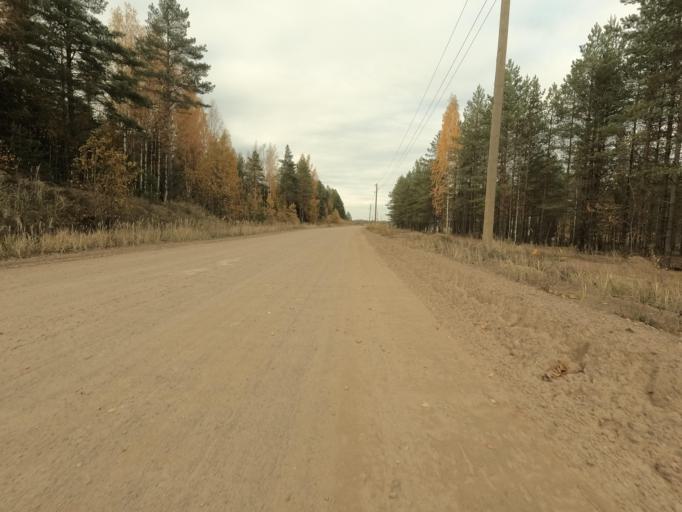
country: RU
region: Leningrad
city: Priladozhskiy
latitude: 59.6973
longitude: 31.3619
